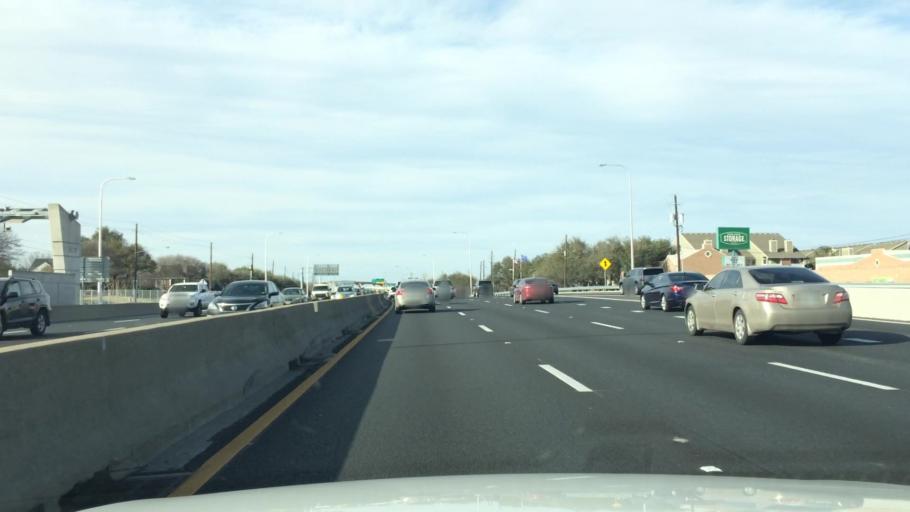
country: US
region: Texas
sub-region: Dallas County
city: Addison
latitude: 33.0012
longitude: -96.8292
